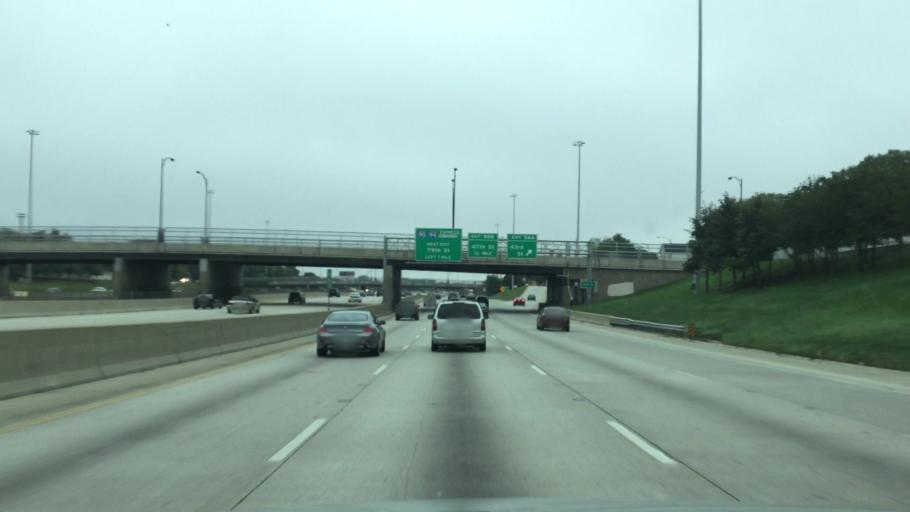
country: US
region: Illinois
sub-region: Cook County
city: Chicago
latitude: 41.8202
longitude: -87.6308
